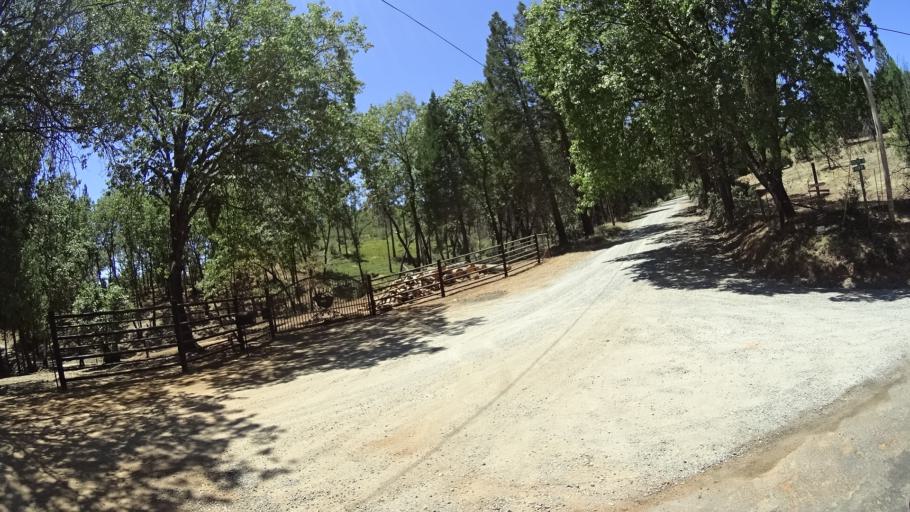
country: US
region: California
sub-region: Calaveras County
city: Mountain Ranch
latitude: 38.2306
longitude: -120.6021
